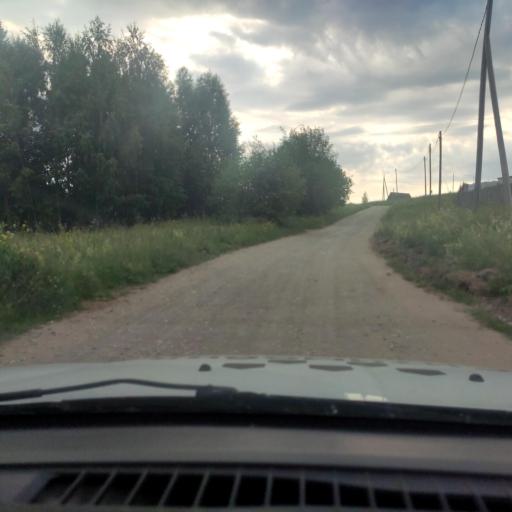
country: RU
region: Perm
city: Polazna
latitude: 58.1724
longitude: 56.3707
